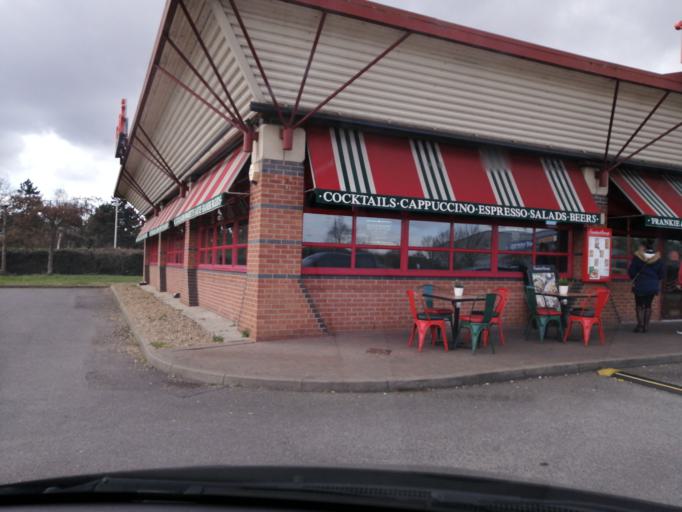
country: GB
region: England
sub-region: Peterborough
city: Peterborough
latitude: 52.5754
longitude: -0.2208
